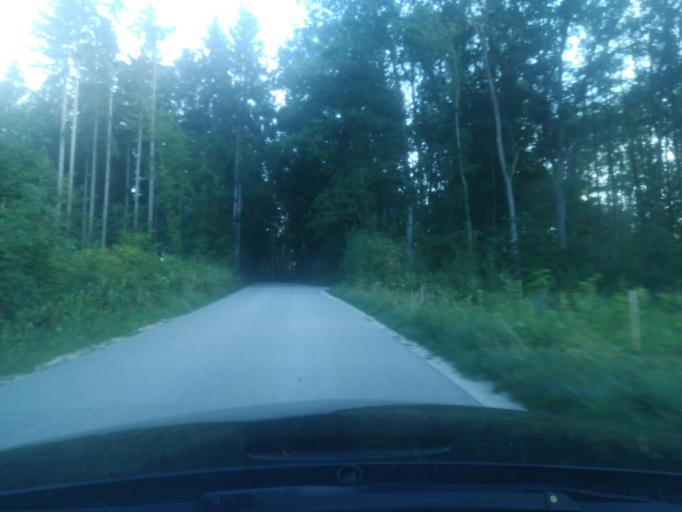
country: AT
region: Upper Austria
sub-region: Wels-Land
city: Marchtrenk
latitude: 48.1617
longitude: 14.1681
